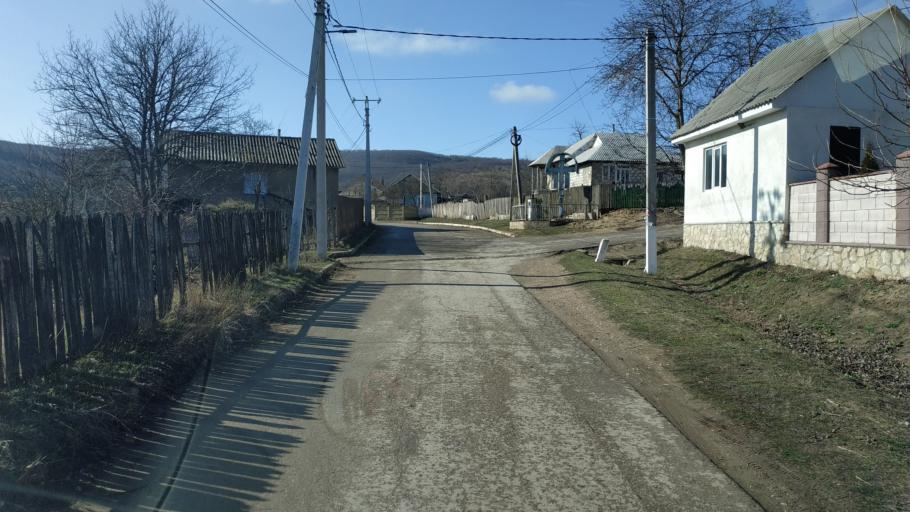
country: MD
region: Hincesti
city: Hincesti
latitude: 46.9225
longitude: 28.6272
